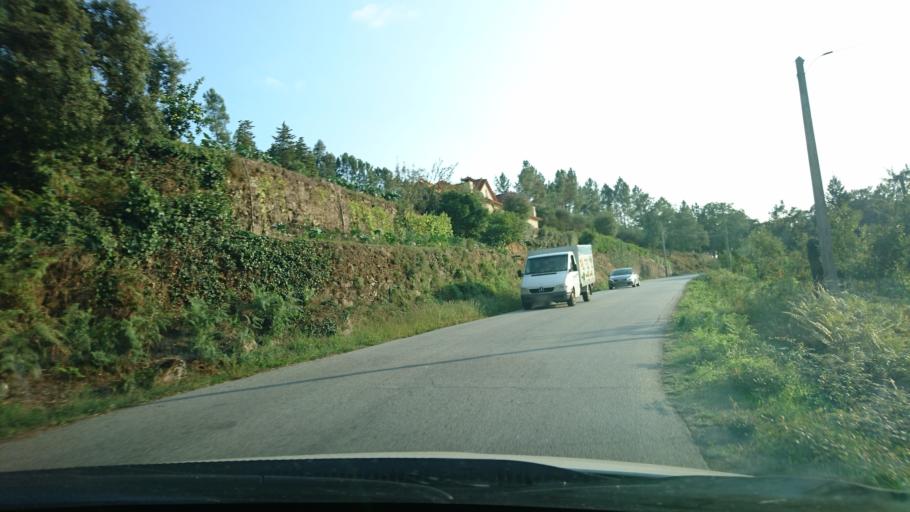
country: PT
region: Vila Real
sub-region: Mondim de Basto
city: Mondim de Basto
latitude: 41.4236
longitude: -7.9360
